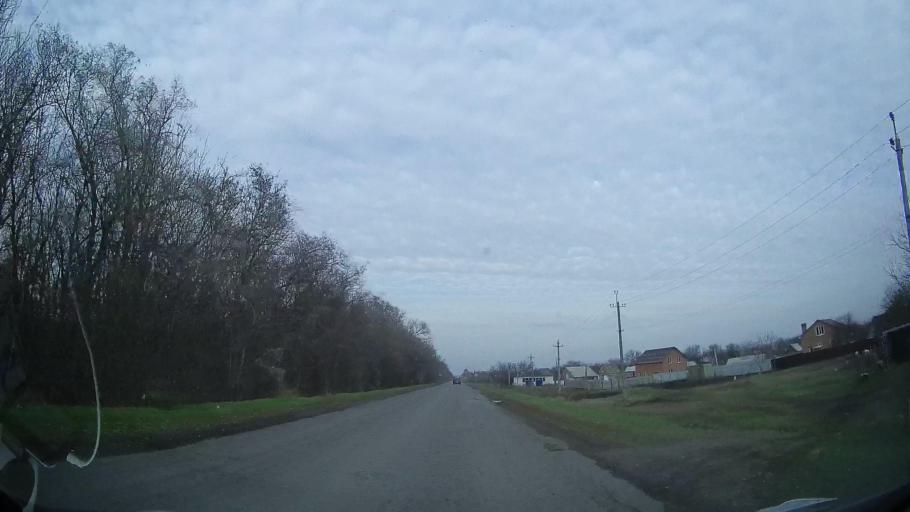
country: RU
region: Rostov
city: Zernograd
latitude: 46.8677
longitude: 40.3283
